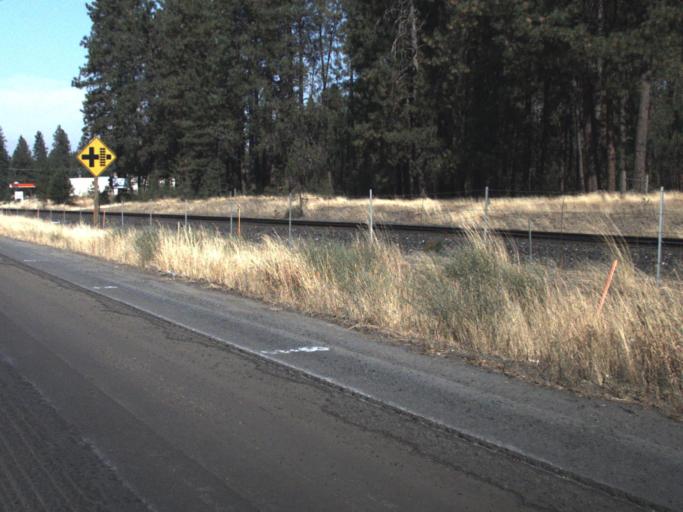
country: US
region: Washington
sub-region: Spokane County
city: Mead
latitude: 47.7990
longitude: -117.3498
